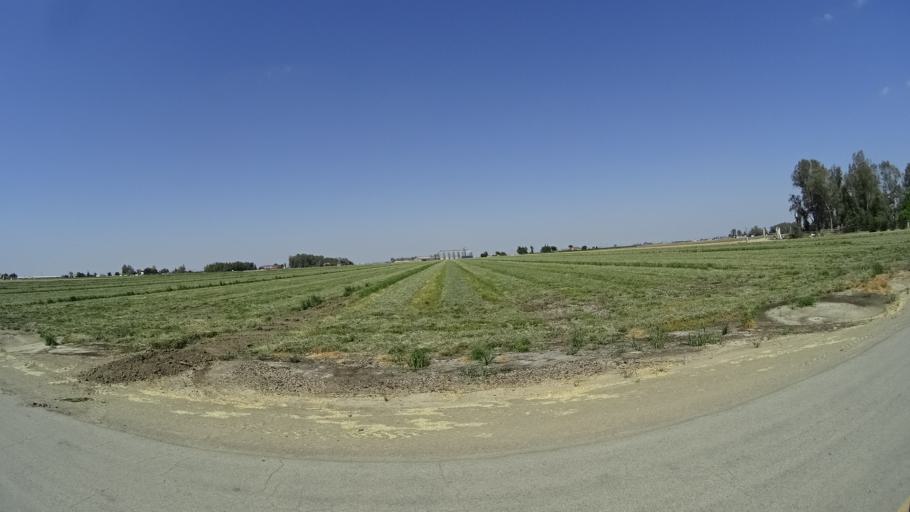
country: US
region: California
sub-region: Kings County
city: Home Garden
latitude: 36.2172
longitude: -119.6279
